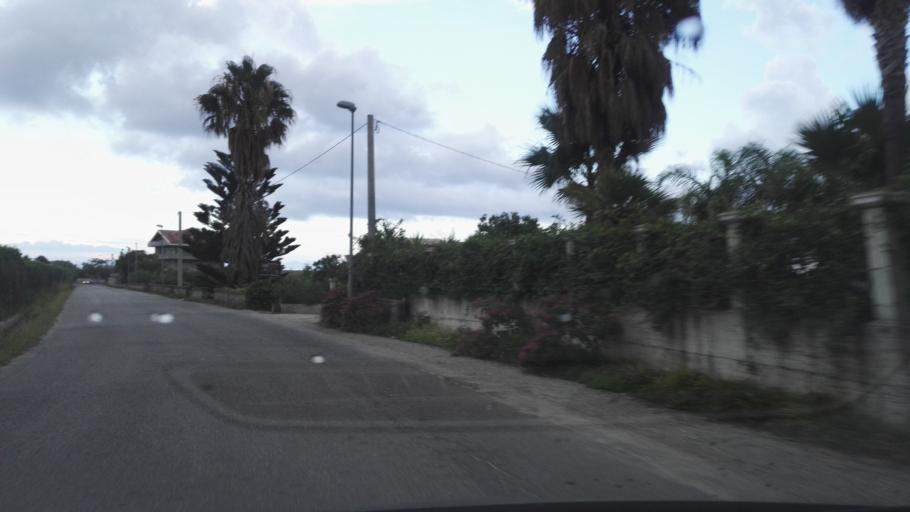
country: IT
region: Calabria
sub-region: Provincia di Reggio Calabria
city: Caulonia Marina
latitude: 38.3596
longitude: 16.4666
